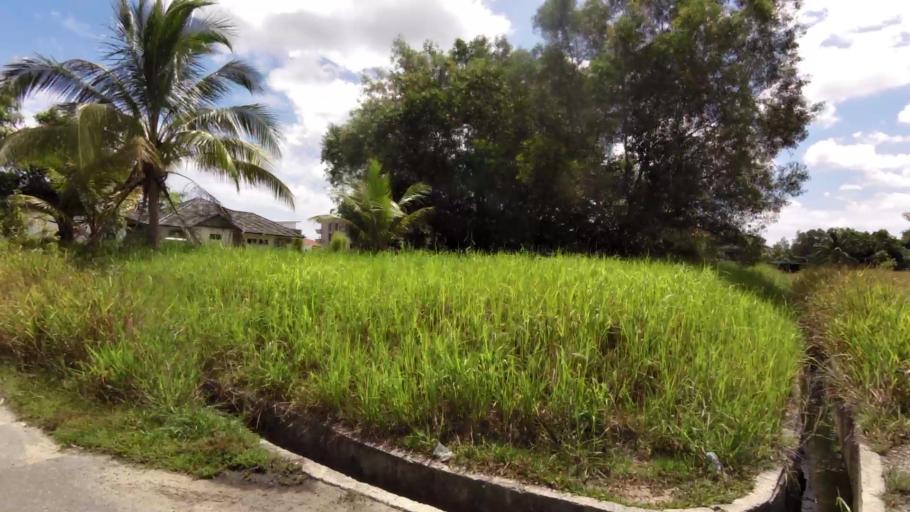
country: BN
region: Brunei and Muara
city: Bandar Seri Begawan
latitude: 4.9411
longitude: 114.9041
